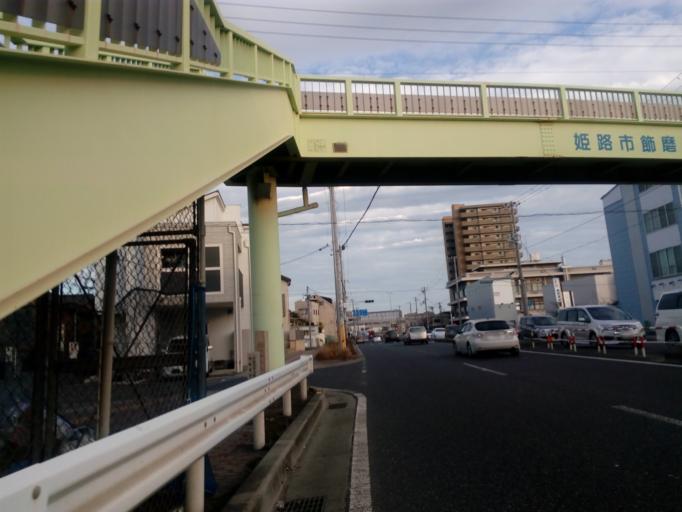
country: JP
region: Hyogo
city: Himeji
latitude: 34.7963
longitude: 134.6698
